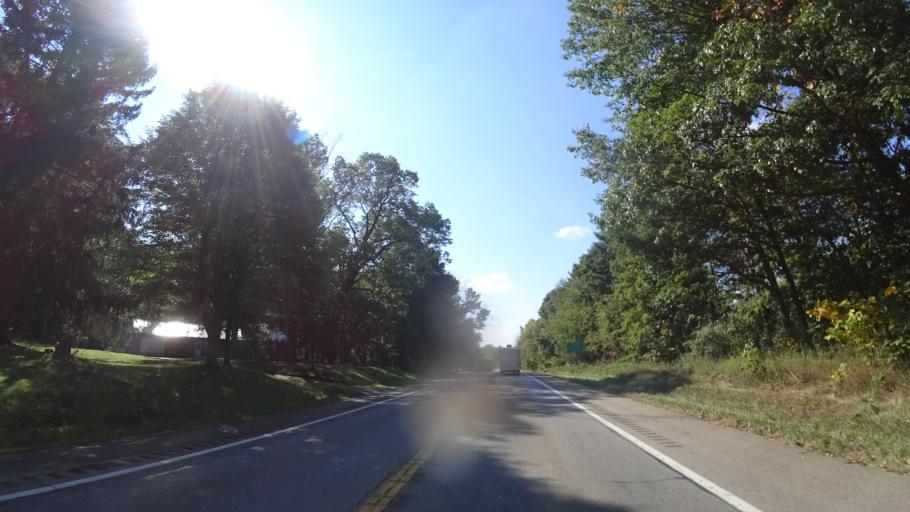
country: US
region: Michigan
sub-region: Calhoun County
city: Homer
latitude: 42.1488
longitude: -84.7978
